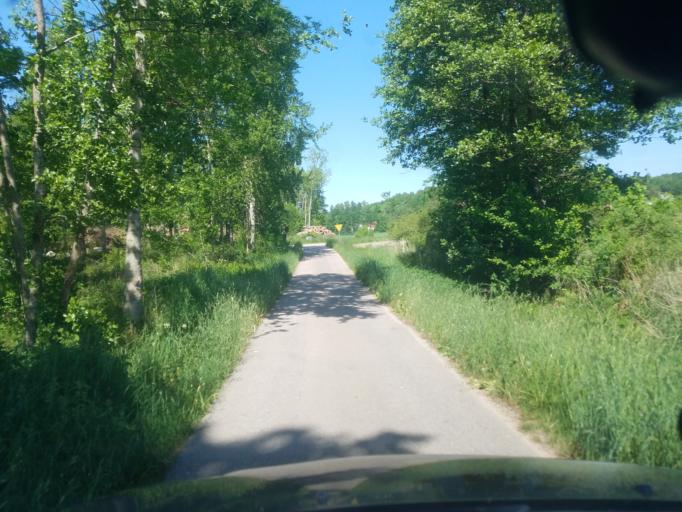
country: SE
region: Vaestra Goetaland
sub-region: Orust
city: Henan
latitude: 58.2654
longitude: 11.5713
